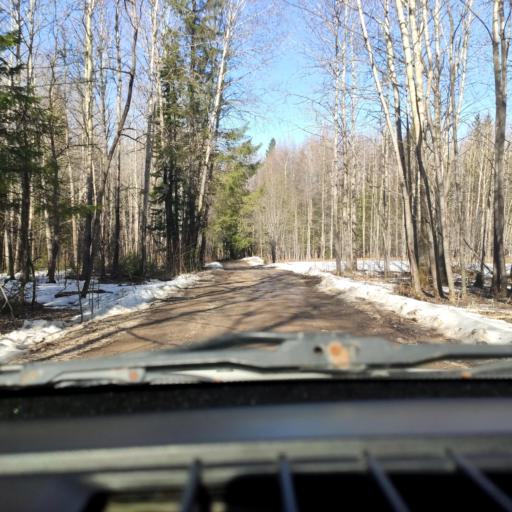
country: RU
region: Perm
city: Kultayevo
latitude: 57.8217
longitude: 55.7979
